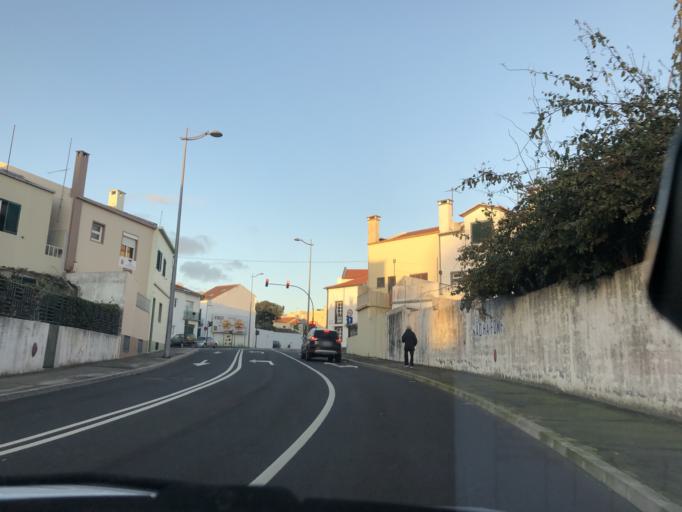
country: PT
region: Azores
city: Ponta Delgada
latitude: 37.7468
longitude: -25.6670
